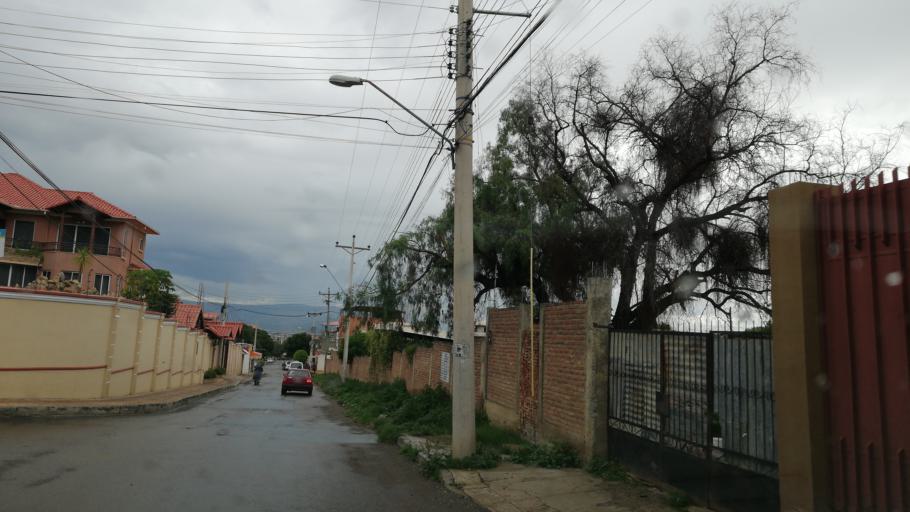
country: BO
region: Cochabamba
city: Cochabamba
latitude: -17.3496
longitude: -66.1797
